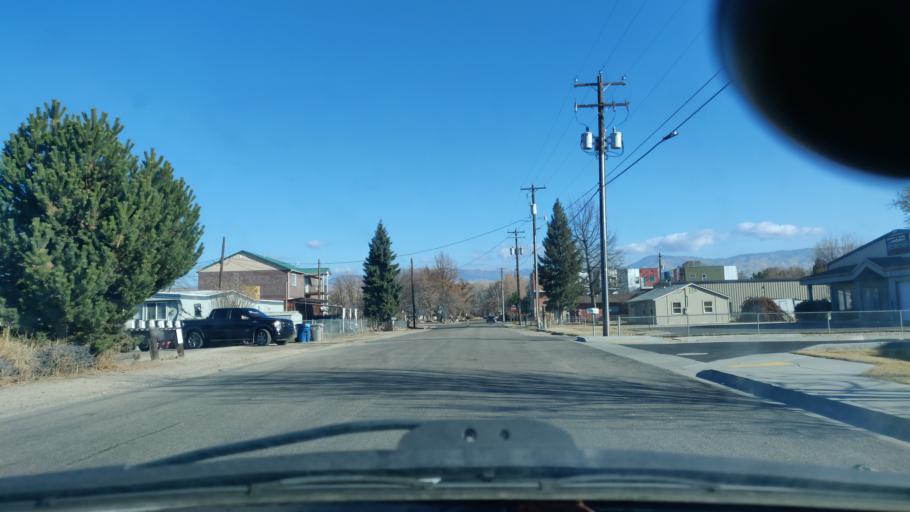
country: US
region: Idaho
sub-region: Ada County
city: Garden City
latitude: 43.6324
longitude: -116.2464
